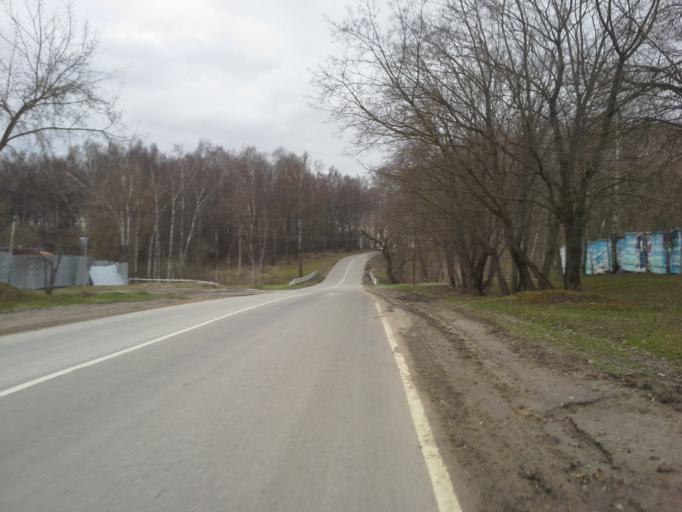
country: RU
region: Moskovskaya
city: Kommunarka
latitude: 55.5226
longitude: 37.4699
